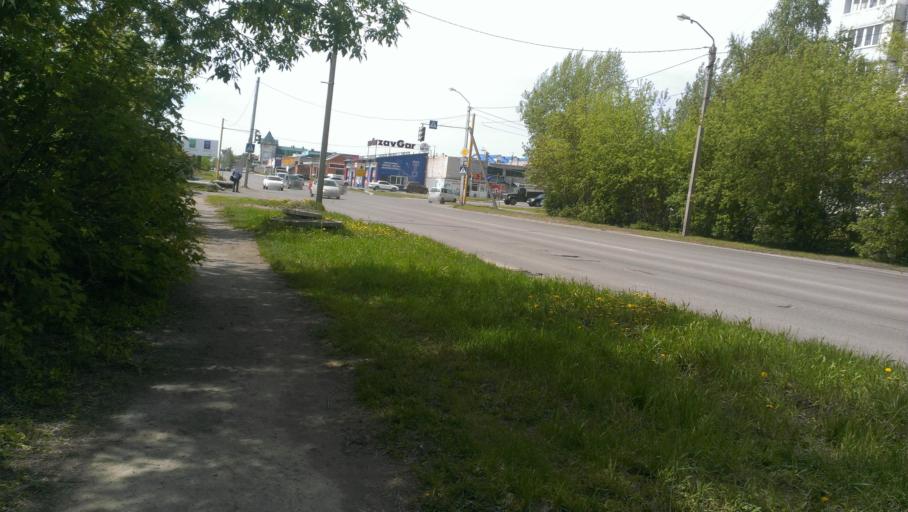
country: RU
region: Altai Krai
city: Novosilikatnyy
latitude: 53.3569
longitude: 83.6599
